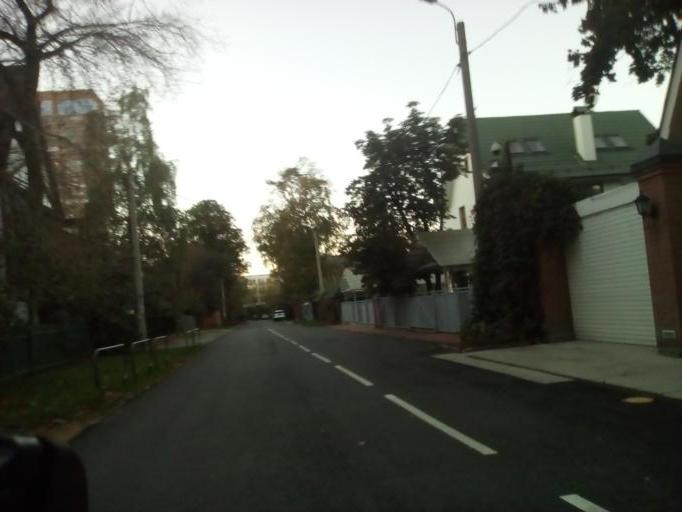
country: RU
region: Moscow
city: Sokol
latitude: 55.8039
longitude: 37.5027
